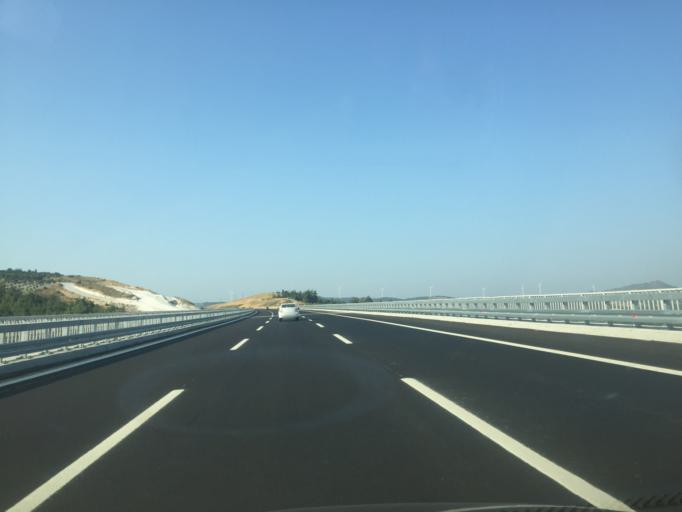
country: TR
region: Manisa
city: Zeytinliova
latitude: 39.0133
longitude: 27.7481
